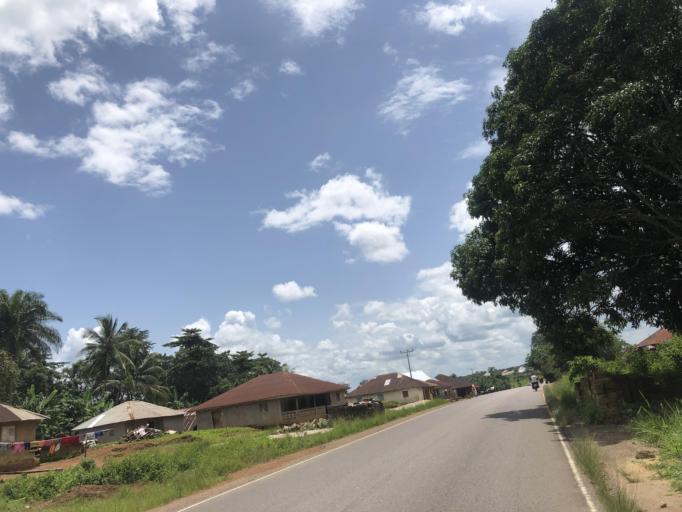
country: SL
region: Northern Province
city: Magburaka
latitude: 8.6954
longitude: -11.9207
